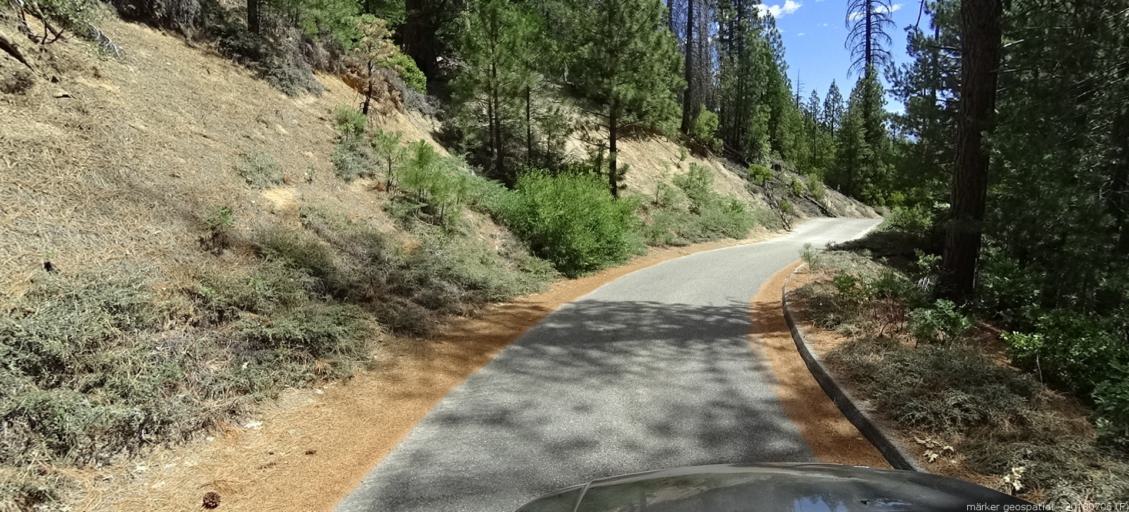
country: US
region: California
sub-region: Madera County
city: Oakhurst
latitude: 37.4102
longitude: -119.4060
